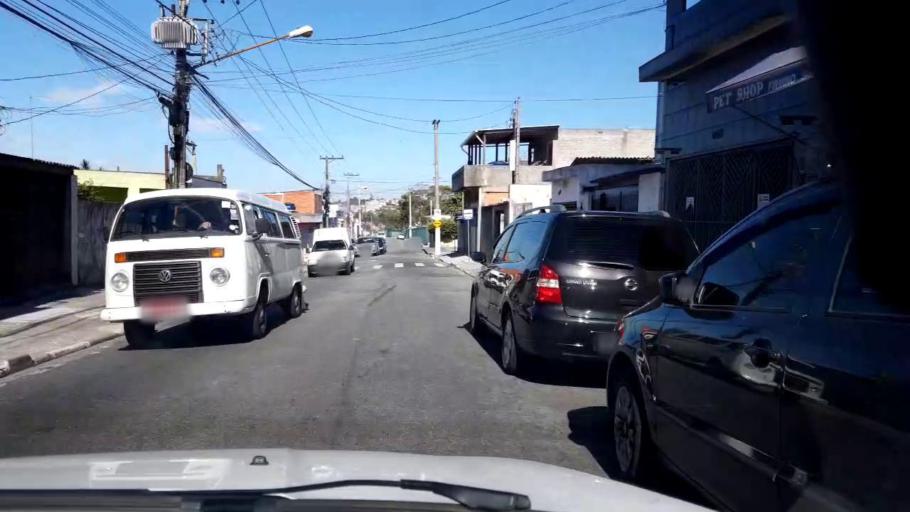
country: BR
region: Sao Paulo
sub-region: Ferraz De Vasconcelos
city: Ferraz de Vasconcelos
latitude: -23.5408
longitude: -46.3803
